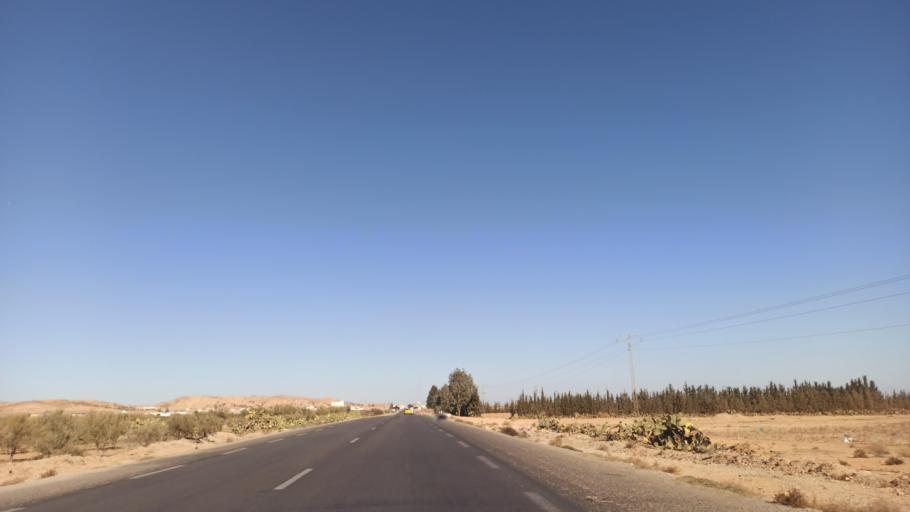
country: TN
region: Sidi Bu Zayd
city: Bi'r al Hufayy
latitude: 34.9063
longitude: 9.1786
